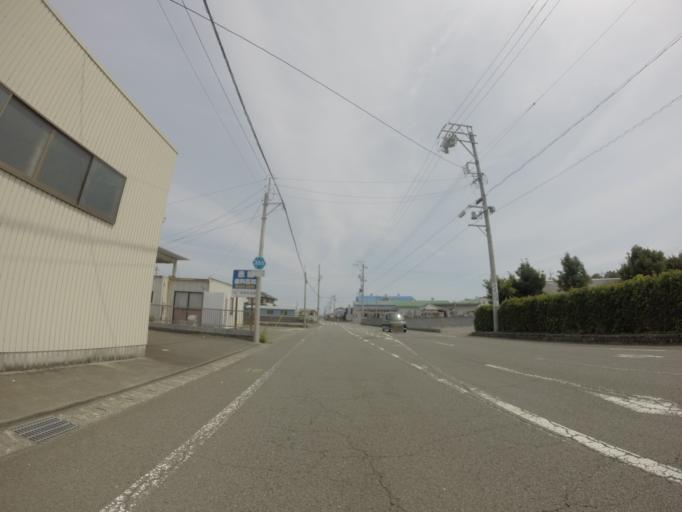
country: JP
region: Shizuoka
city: Yaizu
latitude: 34.7916
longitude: 138.3051
